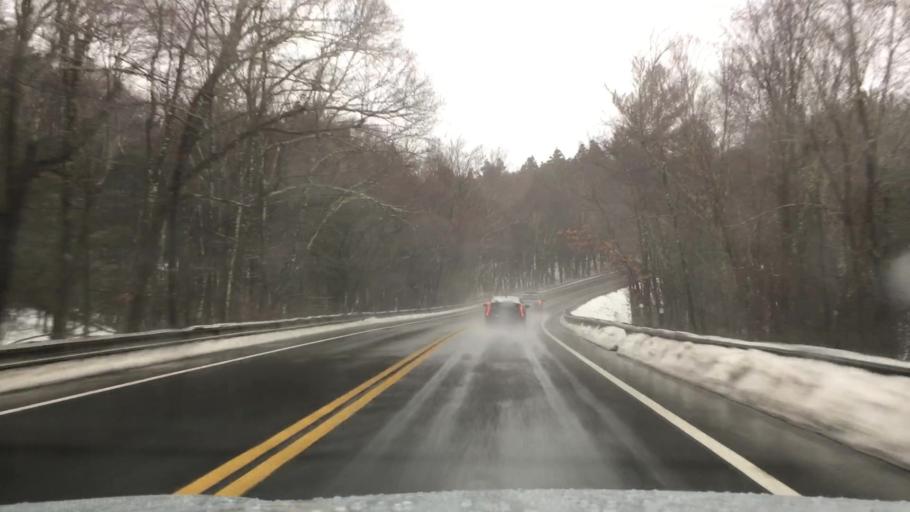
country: US
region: Massachusetts
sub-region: Franklin County
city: Shutesbury
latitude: 42.4379
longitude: -72.3897
